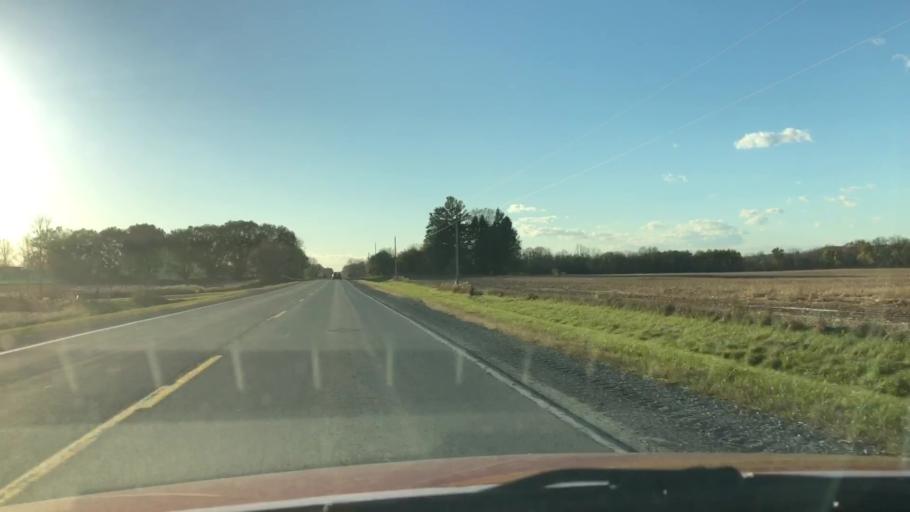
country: US
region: Wisconsin
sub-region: Brown County
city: Oneida
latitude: 44.4442
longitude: -88.1997
